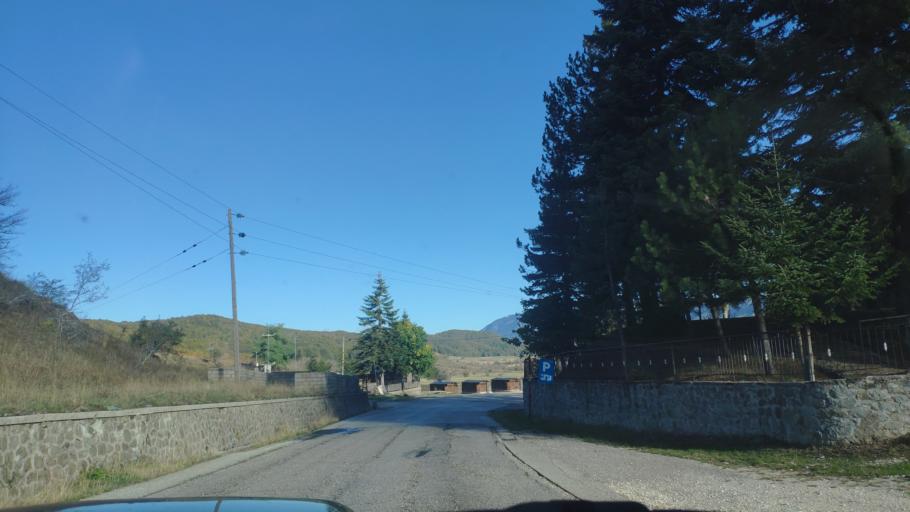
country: GR
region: Epirus
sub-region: Nomos Ioanninon
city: Metsovo
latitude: 39.7839
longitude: 21.1595
